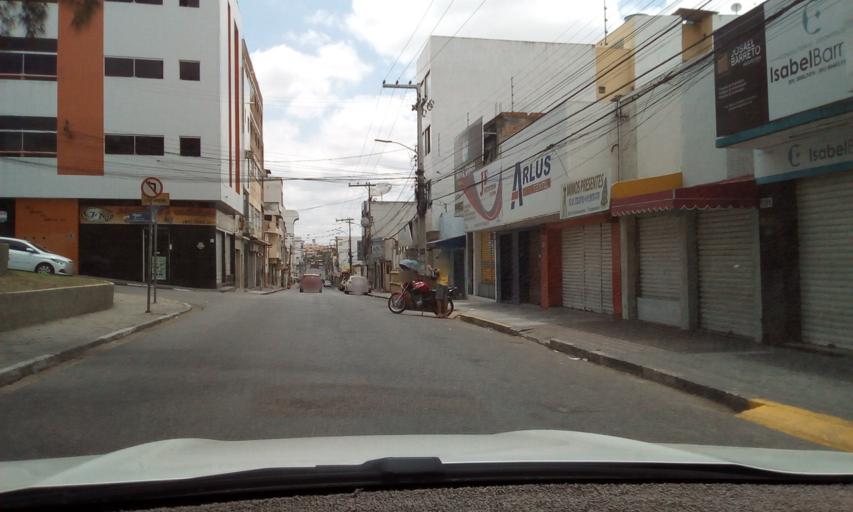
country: BR
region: Pernambuco
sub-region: Caruaru
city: Caruaru
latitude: -8.2880
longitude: -35.9755
